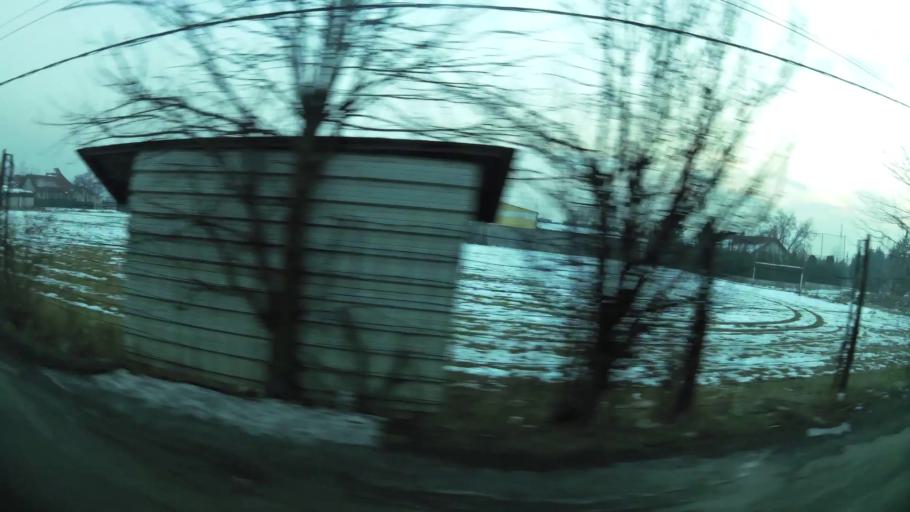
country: MK
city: Creshevo
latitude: 42.0030
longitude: 21.5069
